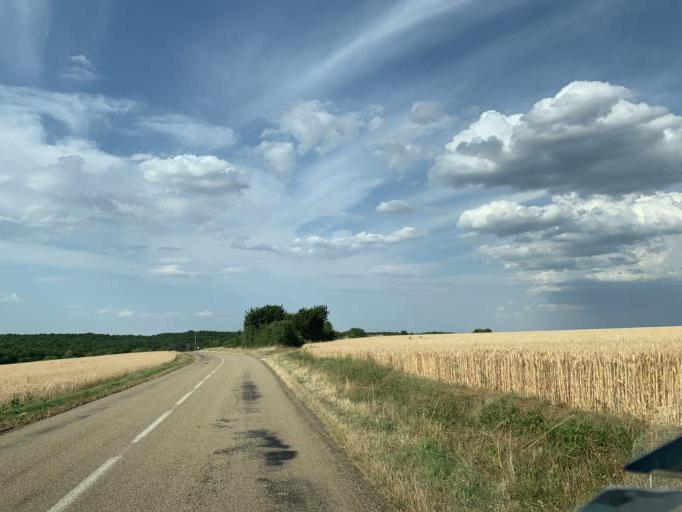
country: FR
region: Bourgogne
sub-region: Departement de l'Yonne
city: Fontenailles
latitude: 47.5271
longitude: 3.3868
